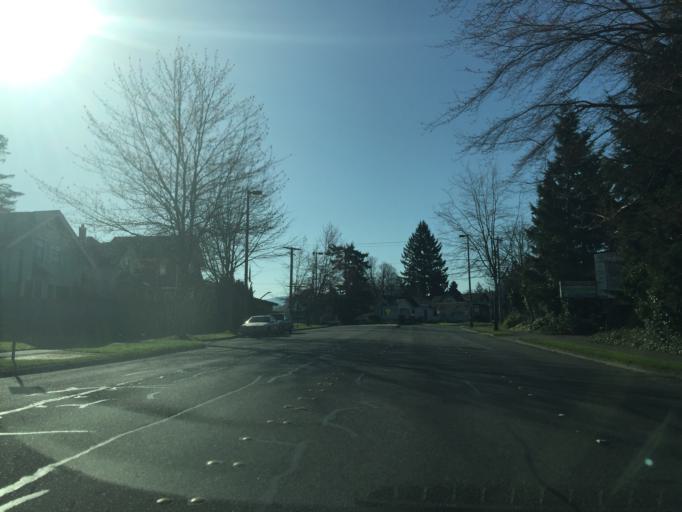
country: US
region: Washington
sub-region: Whatcom County
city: Bellingham
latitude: 48.7420
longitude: -122.4719
